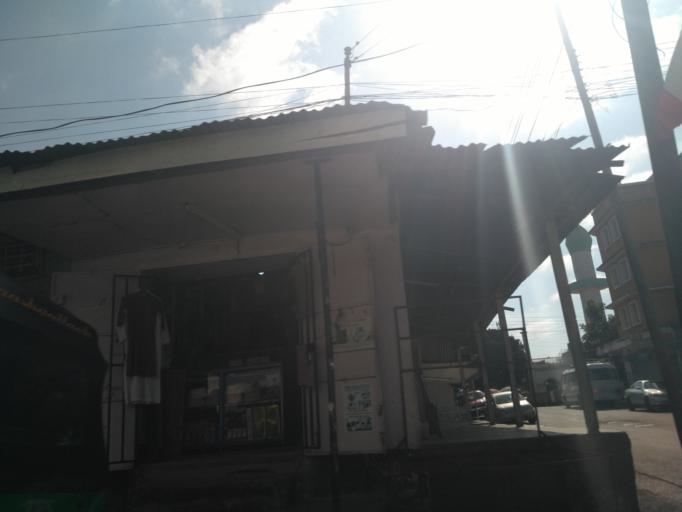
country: TZ
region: Arusha
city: Arusha
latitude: -3.3708
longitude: 36.6869
